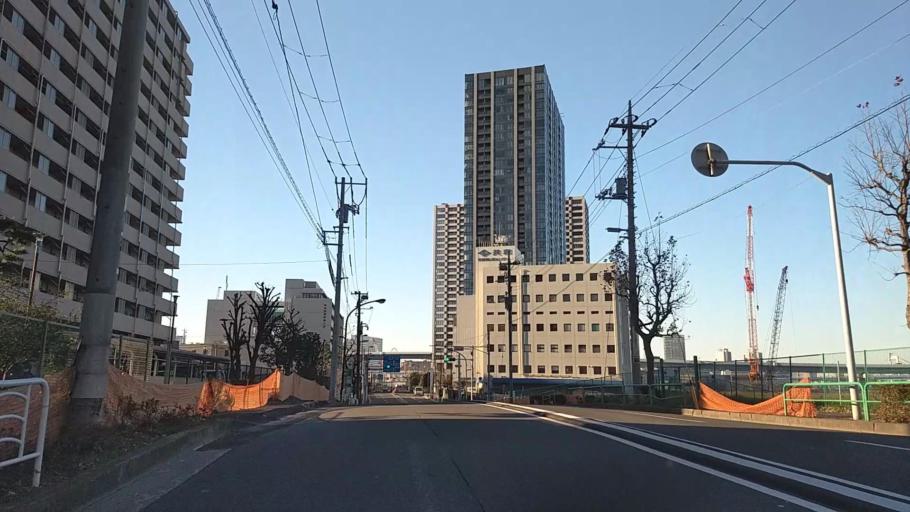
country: JP
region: Tokyo
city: Urayasu
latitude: 35.6438
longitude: 139.7979
